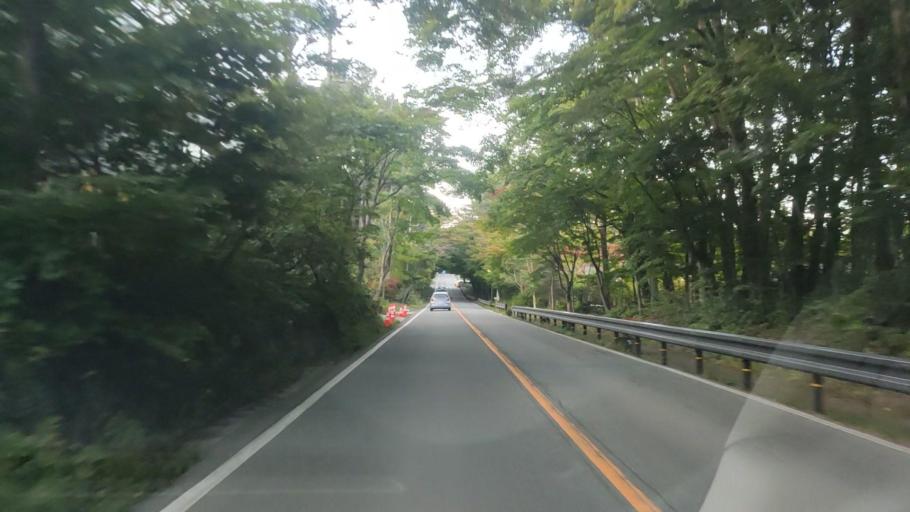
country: JP
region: Nagano
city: Komoro
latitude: 36.3706
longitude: 138.5876
